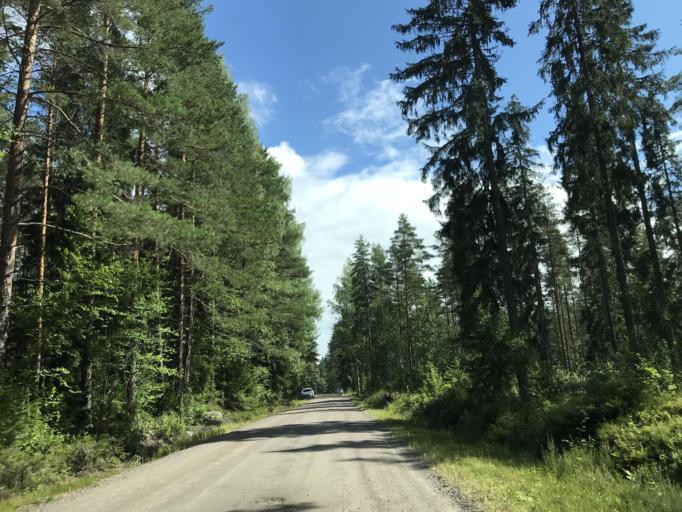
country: FI
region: Uusimaa
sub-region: Helsinki
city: Kaerkoelae
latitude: 60.6257
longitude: 23.7675
